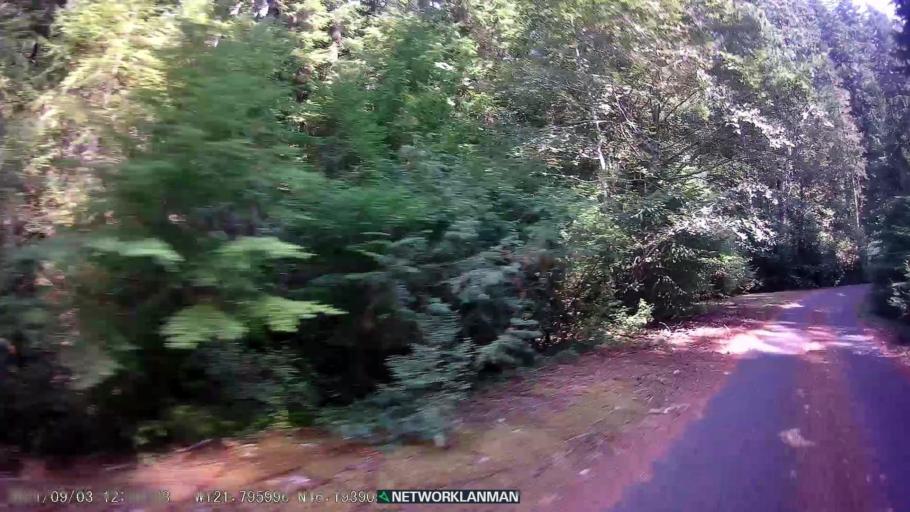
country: US
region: Washington
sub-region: Skamania County
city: Carson
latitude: 46.1937
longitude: -121.7959
